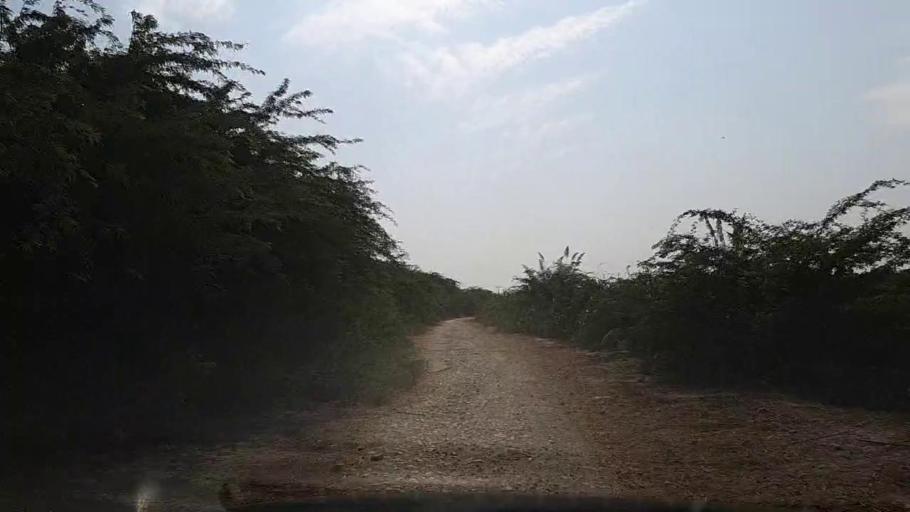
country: PK
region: Sindh
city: Thatta
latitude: 24.7533
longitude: 67.7764
